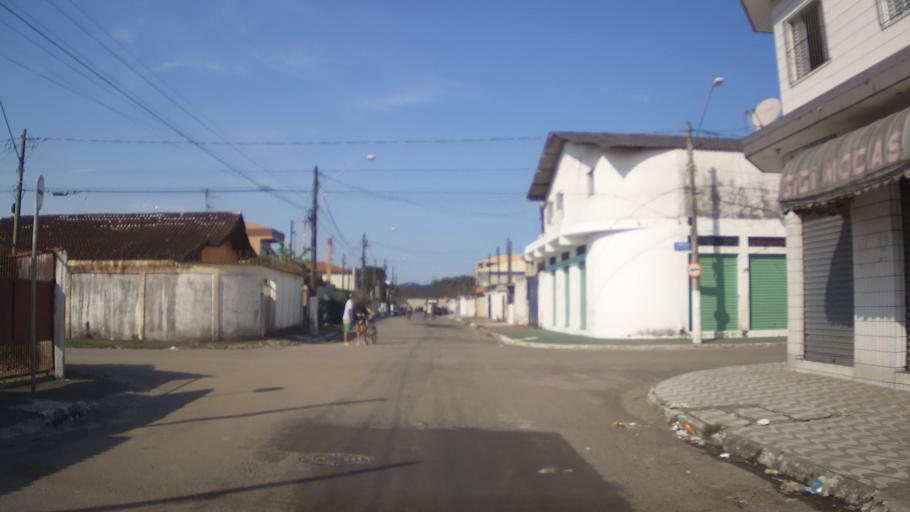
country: BR
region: Sao Paulo
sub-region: Praia Grande
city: Praia Grande
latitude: -24.0060
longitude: -46.4387
